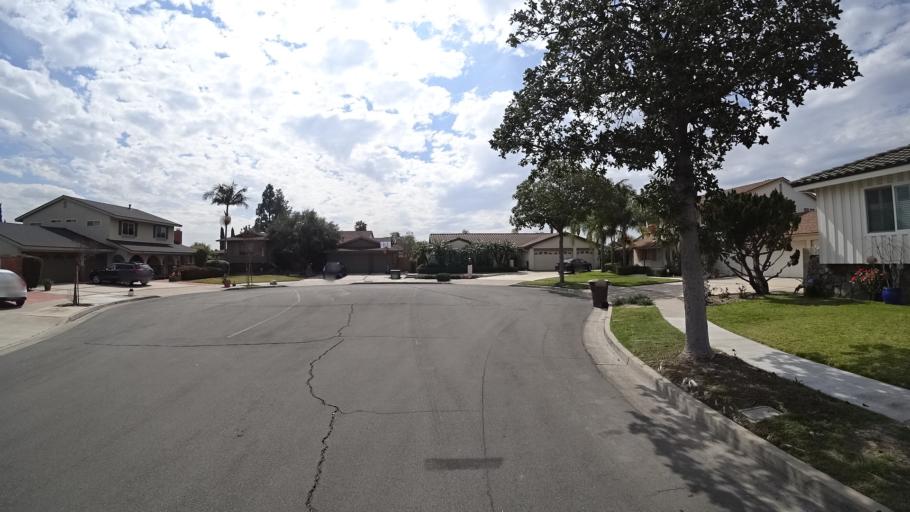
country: US
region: California
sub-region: Orange County
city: Anaheim
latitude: 33.8303
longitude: -117.8854
